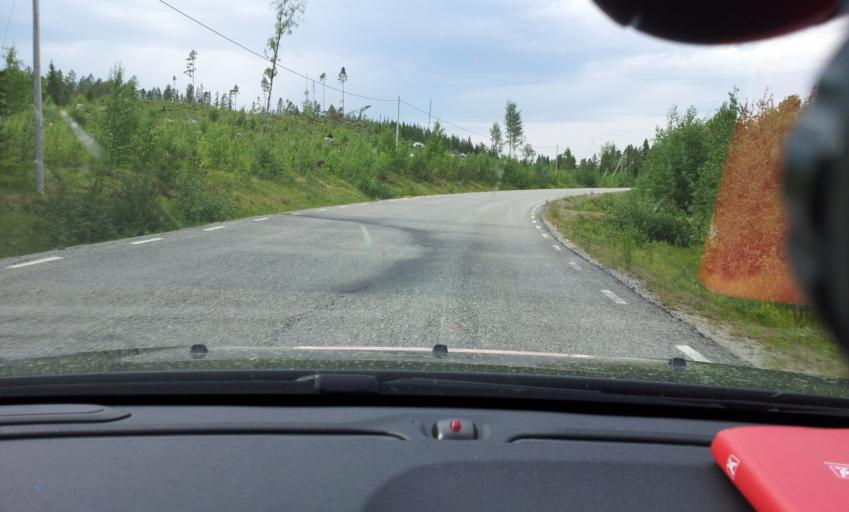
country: SE
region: Jaemtland
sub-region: Bergs Kommun
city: Hoverberg
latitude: 62.6503
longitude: 14.8071
